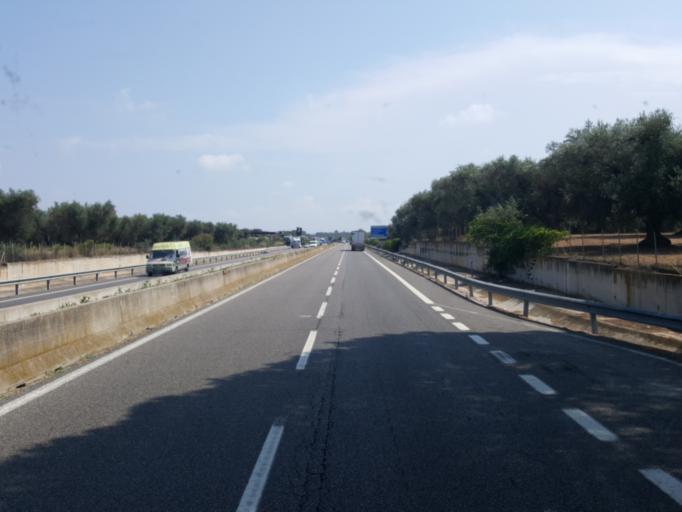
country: IT
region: Apulia
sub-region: Provincia di Brindisi
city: Torchiarolo
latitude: 40.4934
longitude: 18.0367
